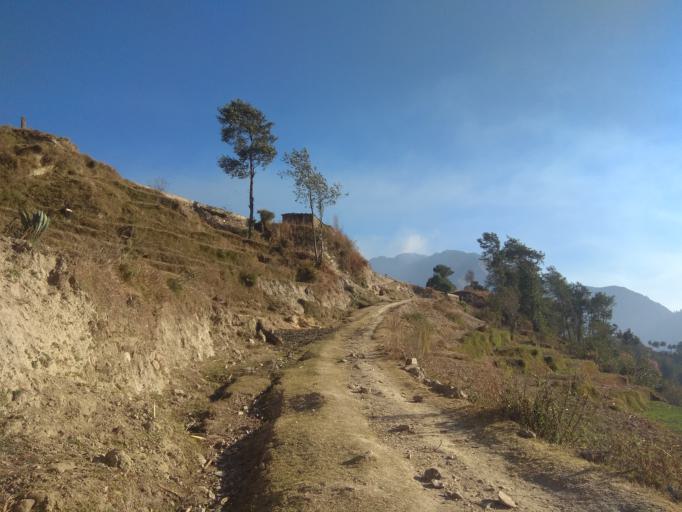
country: NP
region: Far Western
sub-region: Seti Zone
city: Achham
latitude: 29.2487
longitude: 81.6437
